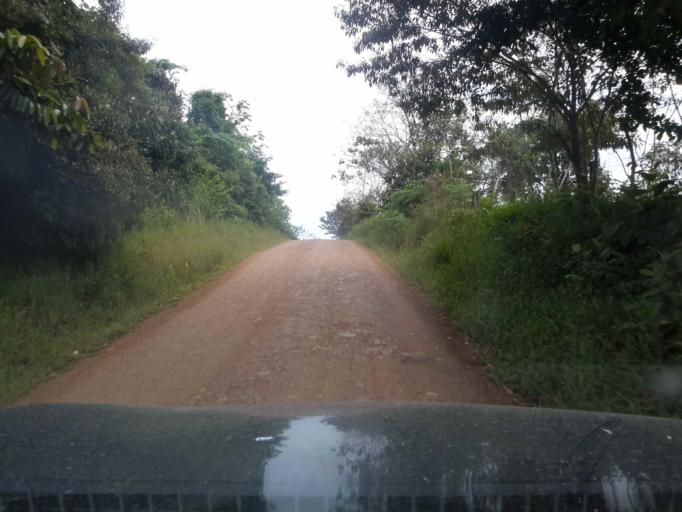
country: CR
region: Alajuela
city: Los Chiles
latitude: 11.0808
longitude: -84.5055
